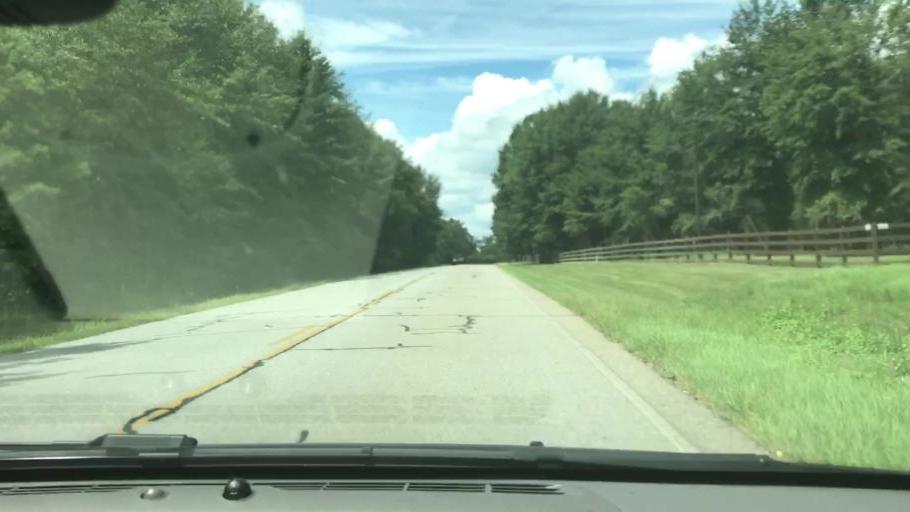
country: US
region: Georgia
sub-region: Stewart County
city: Lumpkin
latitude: 32.1354
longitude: -84.9967
